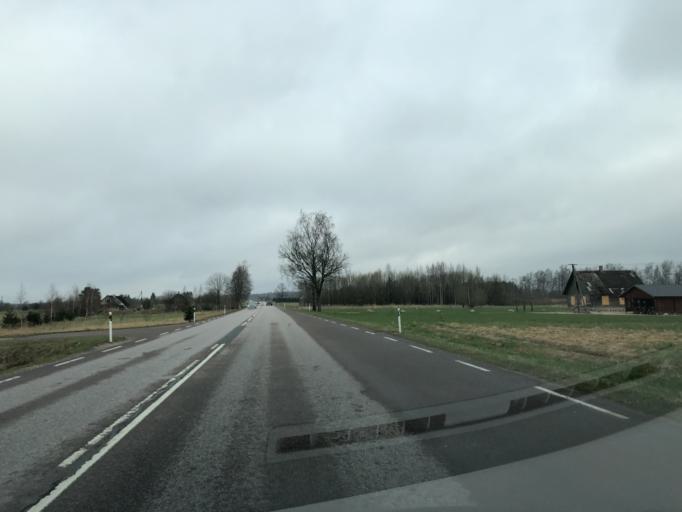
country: EE
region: Jogevamaa
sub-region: Jogeva linn
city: Jogeva
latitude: 58.6746
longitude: 26.4906
